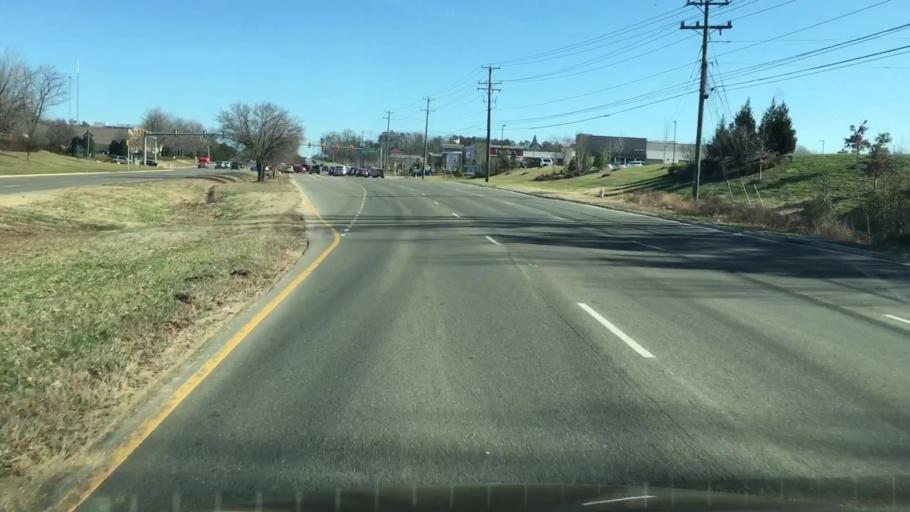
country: US
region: Virginia
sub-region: Chesterfield County
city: Brandermill
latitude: 37.5030
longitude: -77.6303
